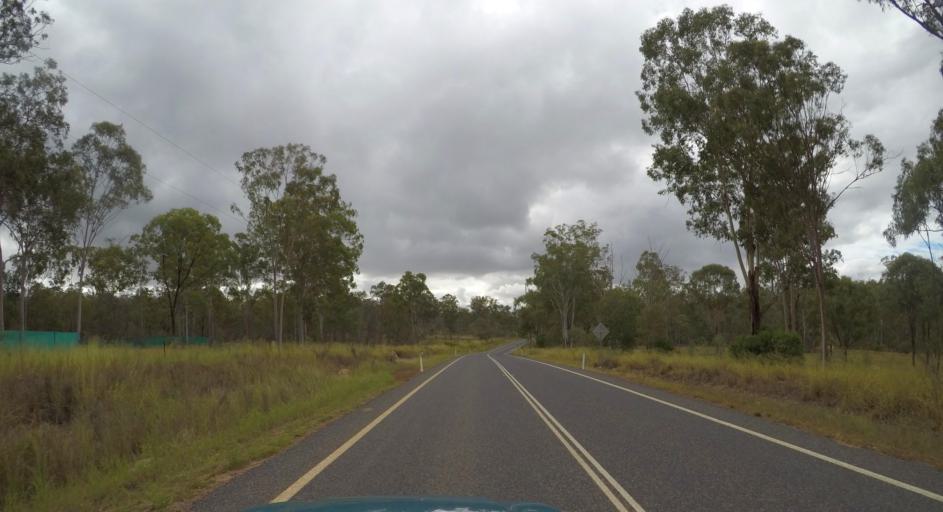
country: AU
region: Queensland
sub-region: North Burnett
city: Gayndah
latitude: -25.3599
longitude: 151.1189
